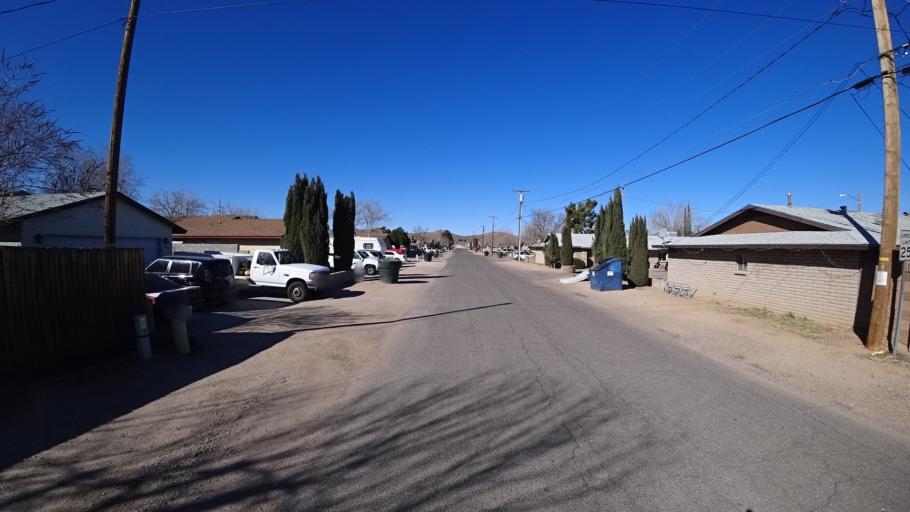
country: US
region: Arizona
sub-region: Mohave County
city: Kingman
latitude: 35.2046
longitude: -114.0296
